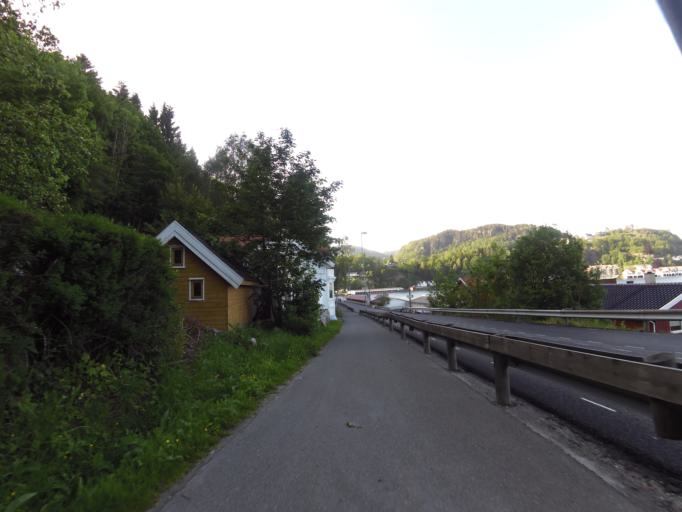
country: NO
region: Vest-Agder
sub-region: Flekkefjord
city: Flekkefjord
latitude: 58.2917
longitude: 6.6481
